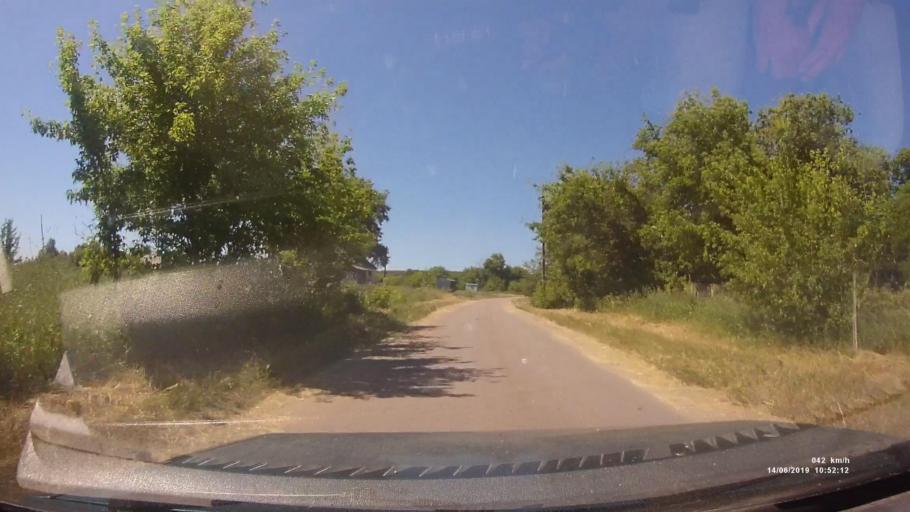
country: RU
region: Rostov
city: Kazanskaya
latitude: 49.8663
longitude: 41.3890
